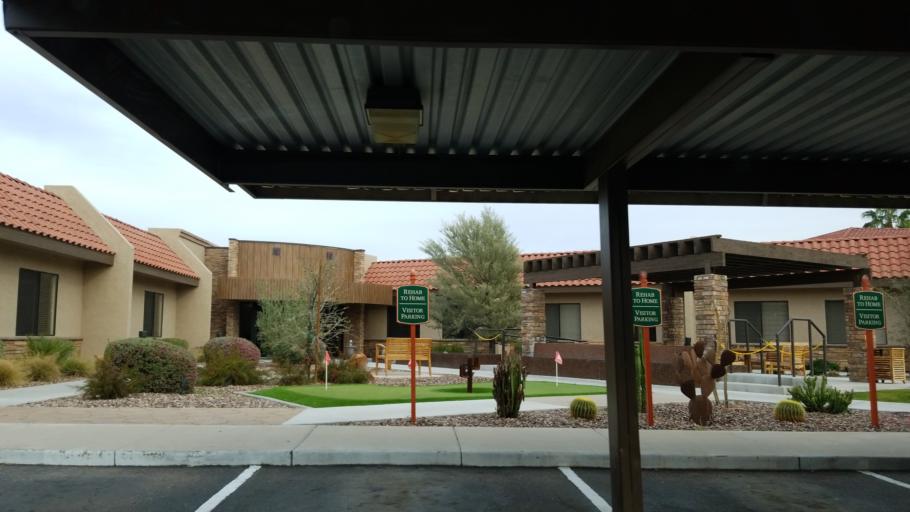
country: US
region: Arizona
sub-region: Maricopa County
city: Paradise Valley
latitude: 33.5863
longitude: -111.9299
